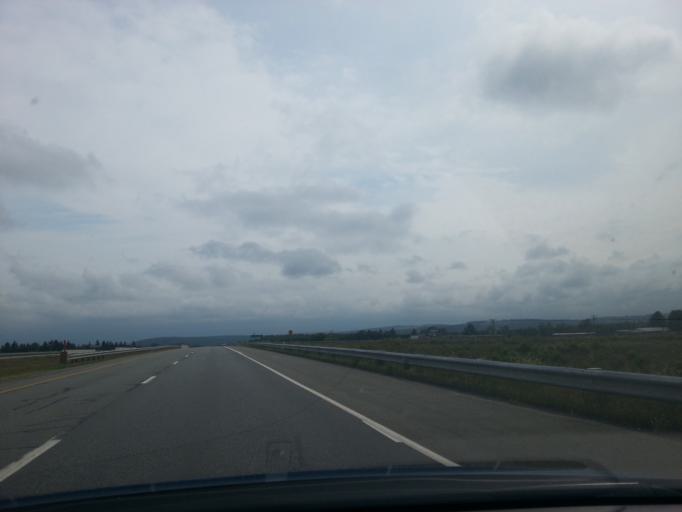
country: US
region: Maine
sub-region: Aroostook County
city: Houlton
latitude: 46.1892
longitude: -67.6103
